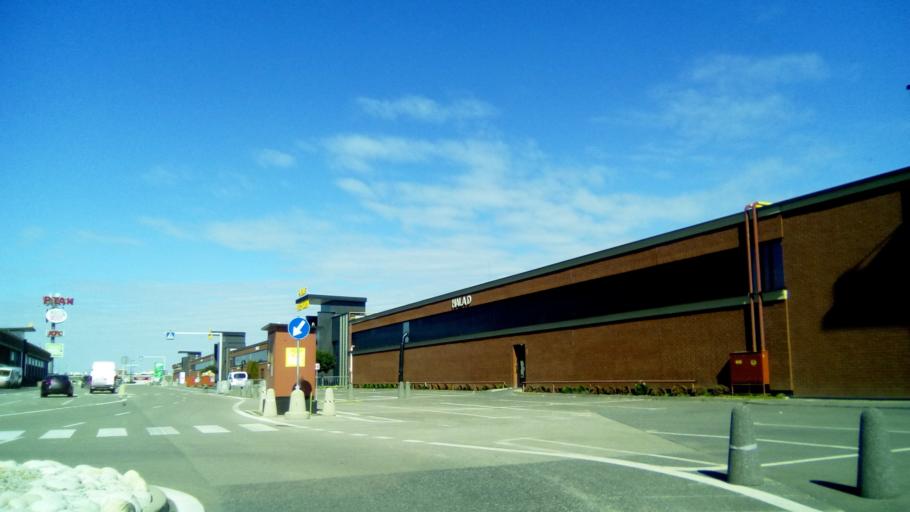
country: PL
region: Lodz Voivodeship
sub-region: Powiat lodzki wschodni
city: Rzgow
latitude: 51.6486
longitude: 19.4928
